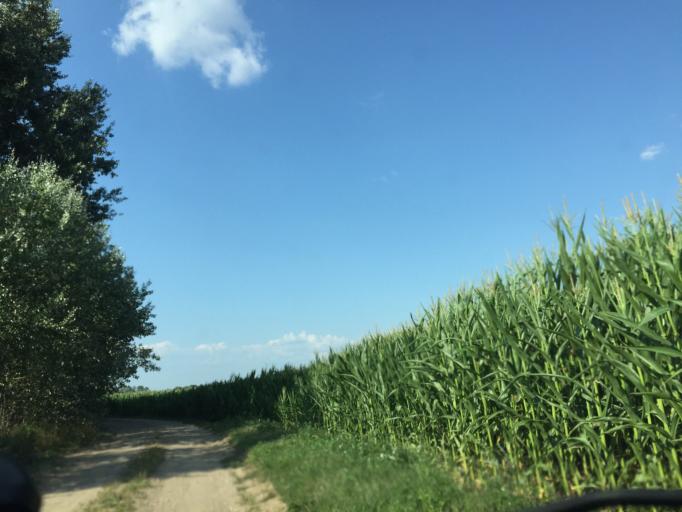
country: LV
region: Jelgava
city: Jelgava
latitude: 56.4686
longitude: 23.6752
